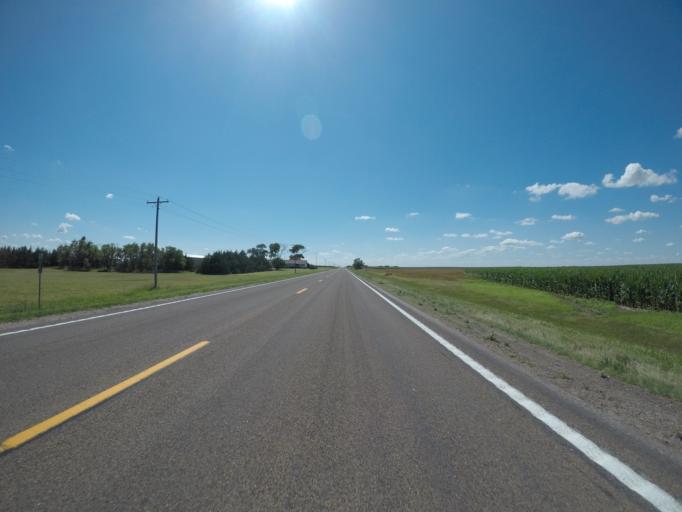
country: US
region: Nebraska
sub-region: Chase County
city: Imperial
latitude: 40.5375
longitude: -101.7851
